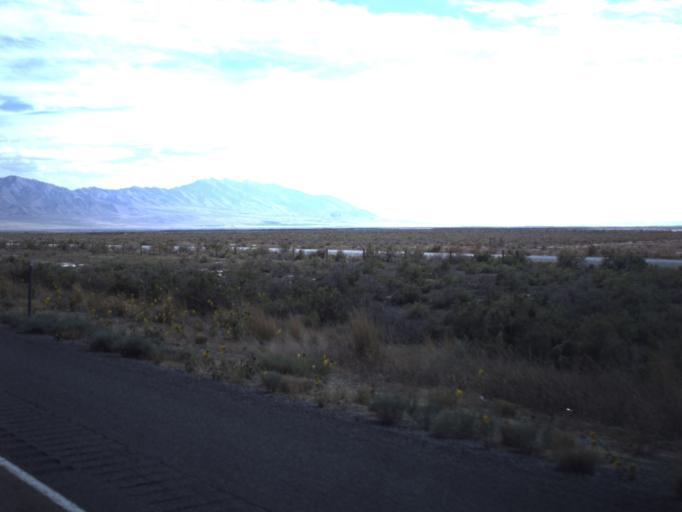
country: US
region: Utah
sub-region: Tooele County
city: Grantsville
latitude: 40.7710
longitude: -112.7967
